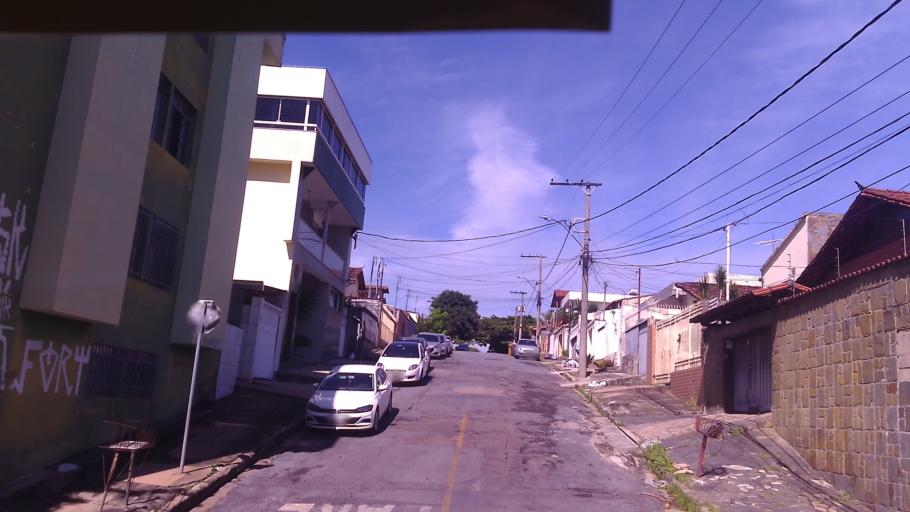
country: BR
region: Minas Gerais
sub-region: Contagem
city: Contagem
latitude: -19.9282
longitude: -43.9975
